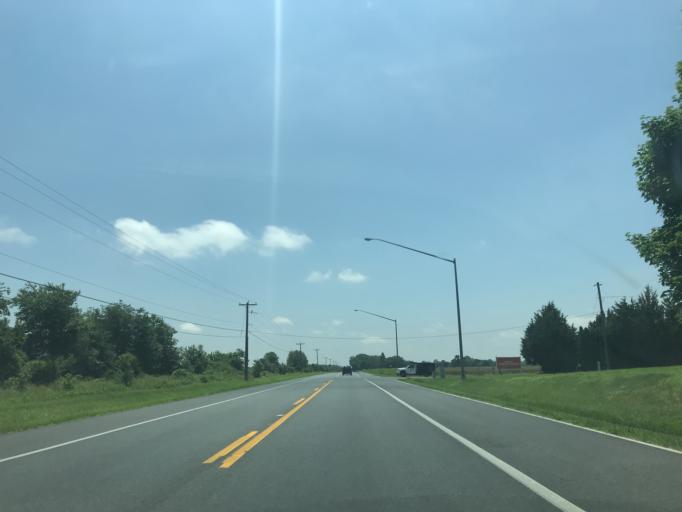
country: US
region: Maryland
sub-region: Dorchester County
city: Hurlock
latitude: 38.6074
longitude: -75.9018
